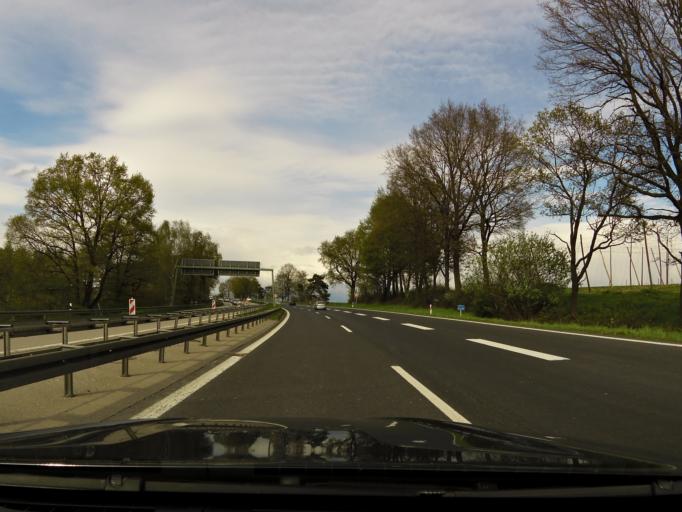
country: DE
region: Bavaria
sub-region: Upper Bavaria
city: Wolnzach
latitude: 48.5824
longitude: 11.5967
